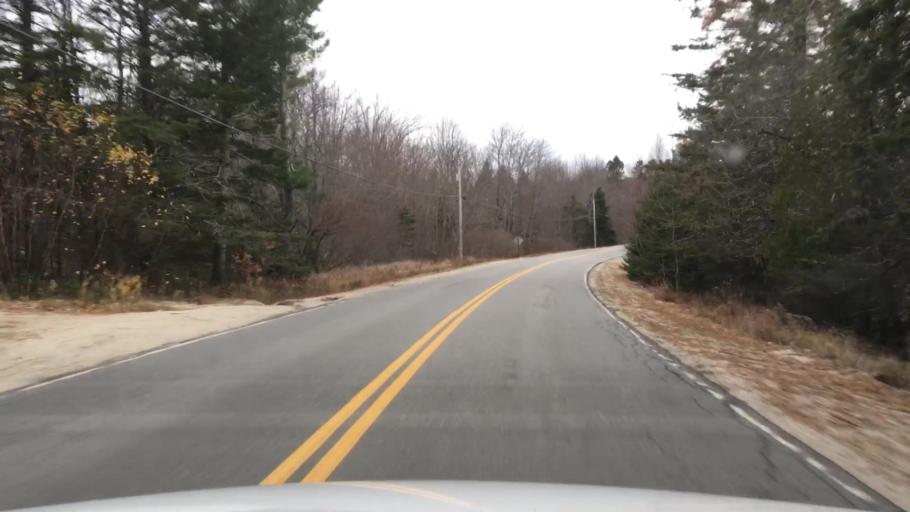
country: US
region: Maine
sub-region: Hancock County
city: Penobscot
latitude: 44.4322
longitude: -68.6297
